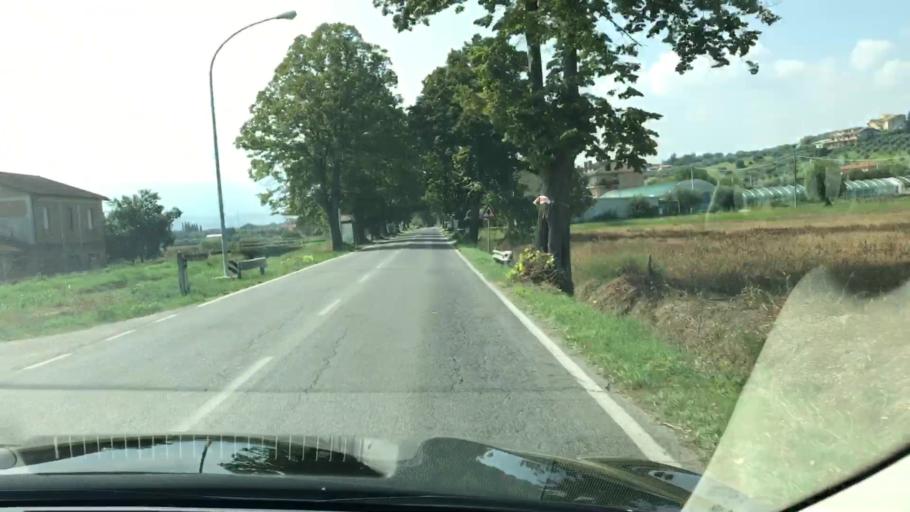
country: IT
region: The Marches
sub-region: Provincia di Ascoli Piceno
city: Pagliare
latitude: 42.8782
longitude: 13.7819
